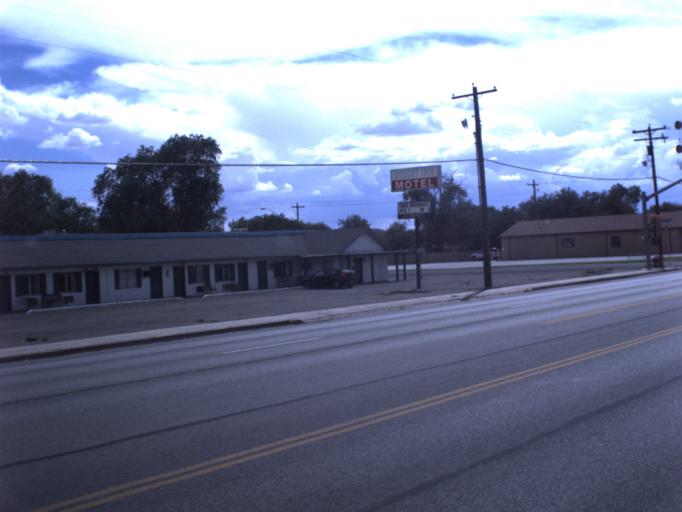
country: US
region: Utah
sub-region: Carbon County
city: East Carbon City
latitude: 38.9956
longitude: -110.1601
